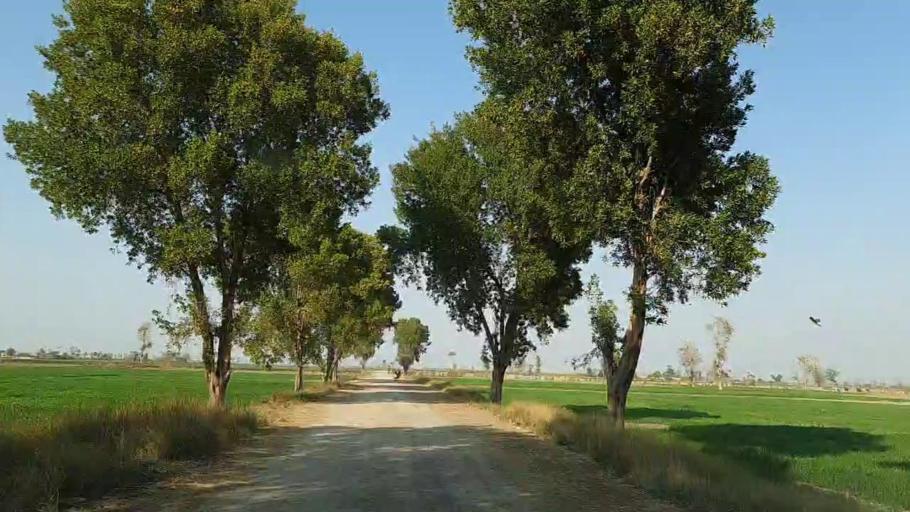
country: PK
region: Sindh
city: Daur
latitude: 26.4855
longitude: 68.2973
